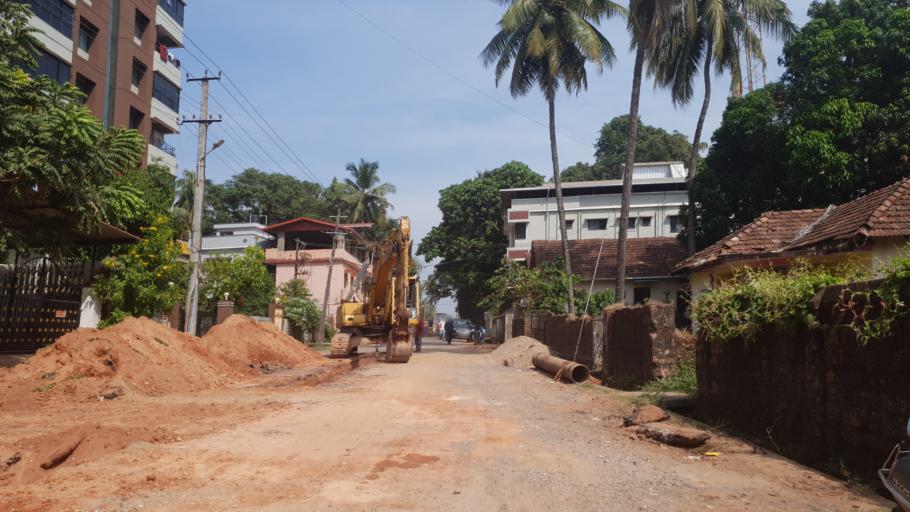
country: IN
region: Karnataka
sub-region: Dakshina Kannada
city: Ullal
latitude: 12.8467
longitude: 74.8435
